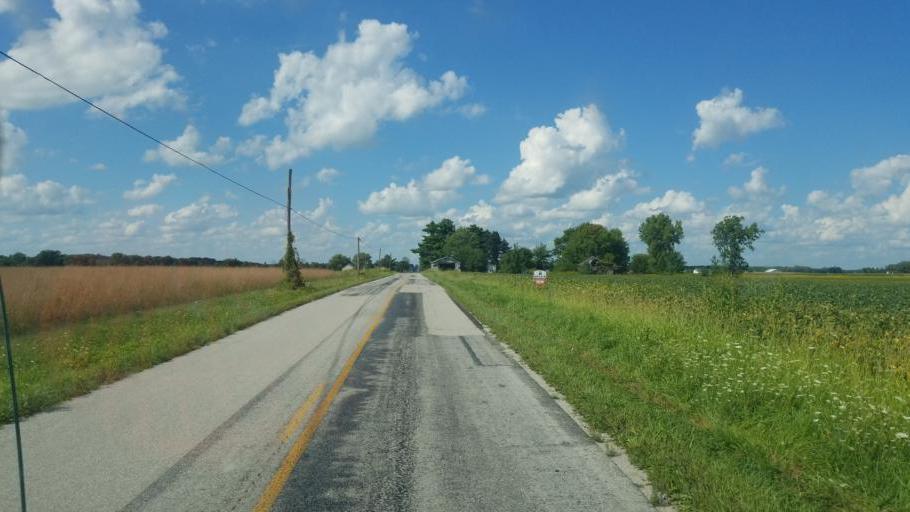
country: US
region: Ohio
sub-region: Union County
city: Richwood
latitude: 40.5144
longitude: -83.3836
